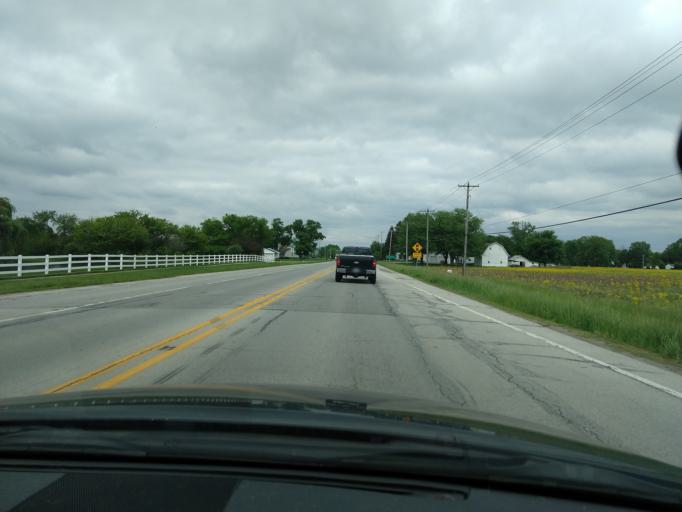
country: US
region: Indiana
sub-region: Hamilton County
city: Westfield
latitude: 40.0429
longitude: -86.0941
